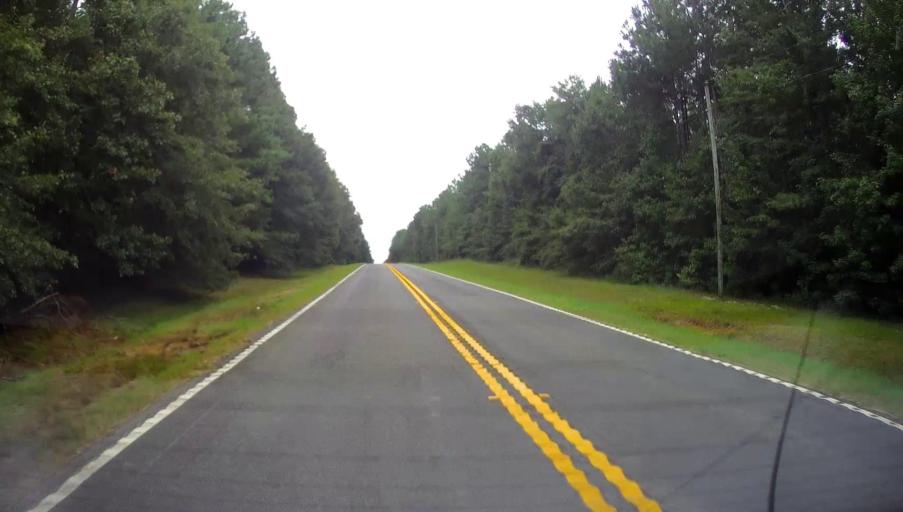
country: US
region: Georgia
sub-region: Dooly County
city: Unadilla
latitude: 32.2911
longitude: -83.8585
